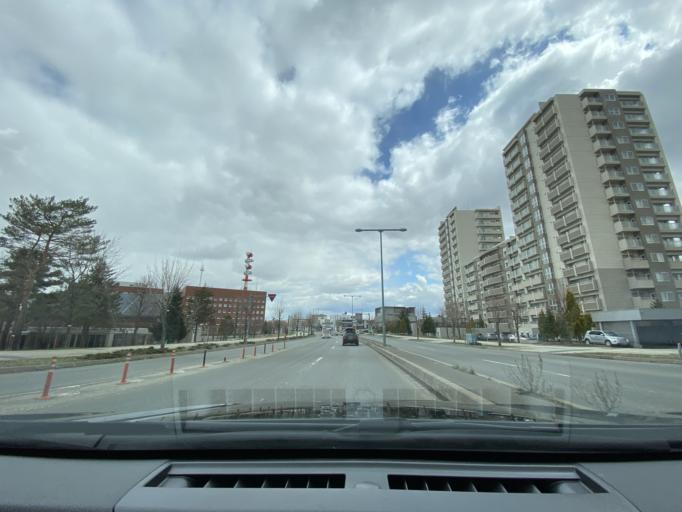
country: JP
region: Hokkaido
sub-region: Asahikawa-shi
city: Asahikawa
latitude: 43.7560
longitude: 142.3714
